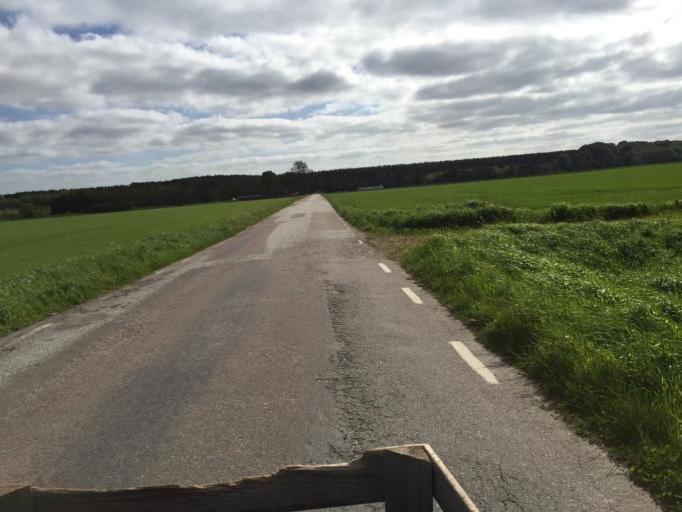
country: SE
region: Skane
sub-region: Sjobo Kommun
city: Blentarp
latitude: 55.6669
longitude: 13.6221
